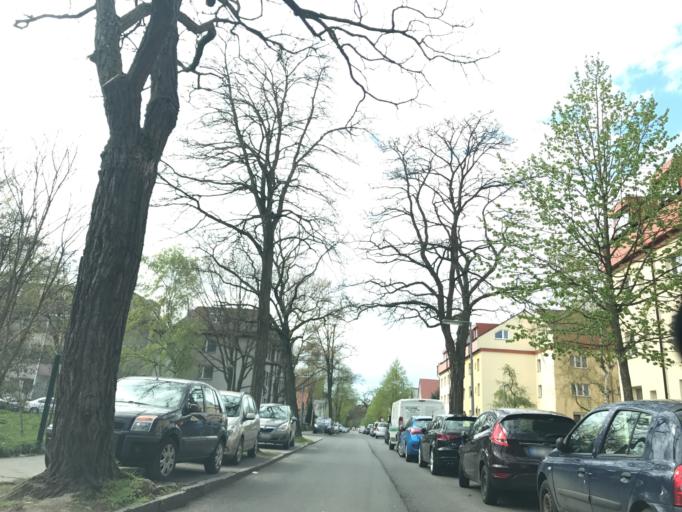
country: DE
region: Berlin
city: Reinickendorf
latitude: 52.5738
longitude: 13.3238
